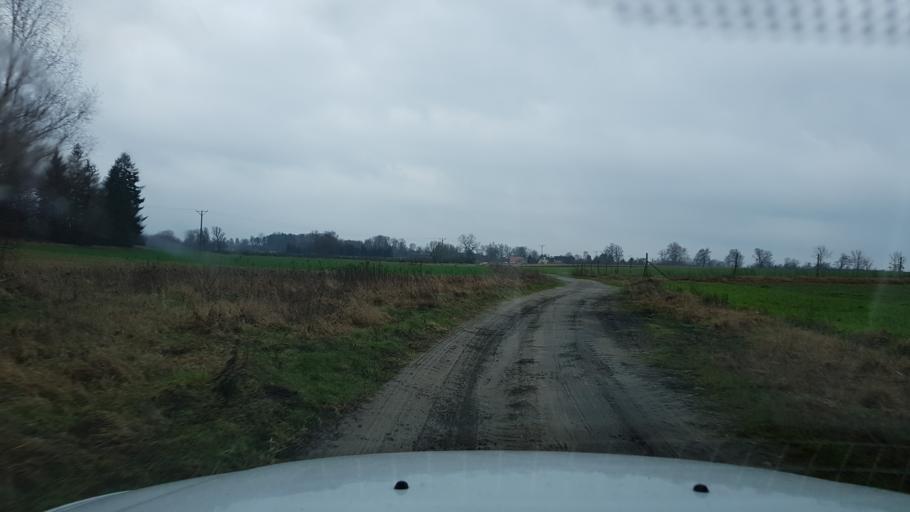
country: PL
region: West Pomeranian Voivodeship
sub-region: Powiat gryficki
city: Brojce
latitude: 53.9745
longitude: 15.3008
